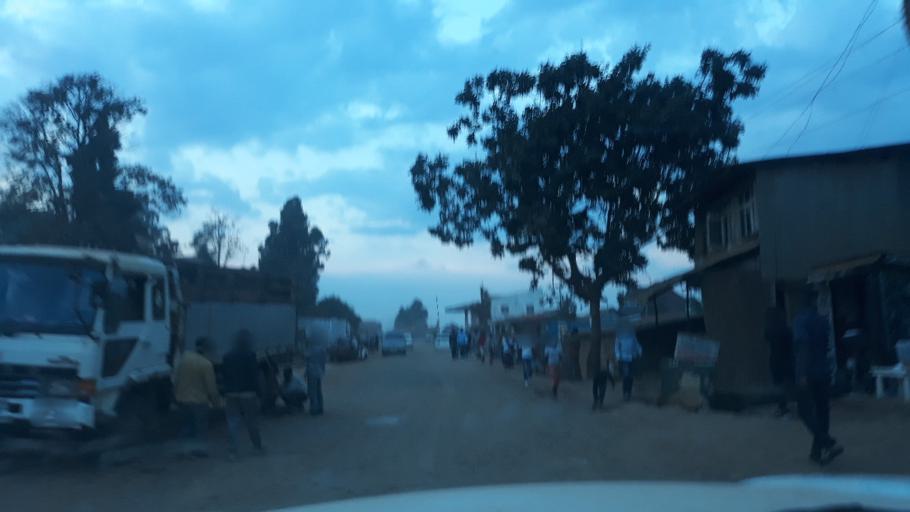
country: CD
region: South Kivu
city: Bukavu
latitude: -2.5426
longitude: 28.8637
